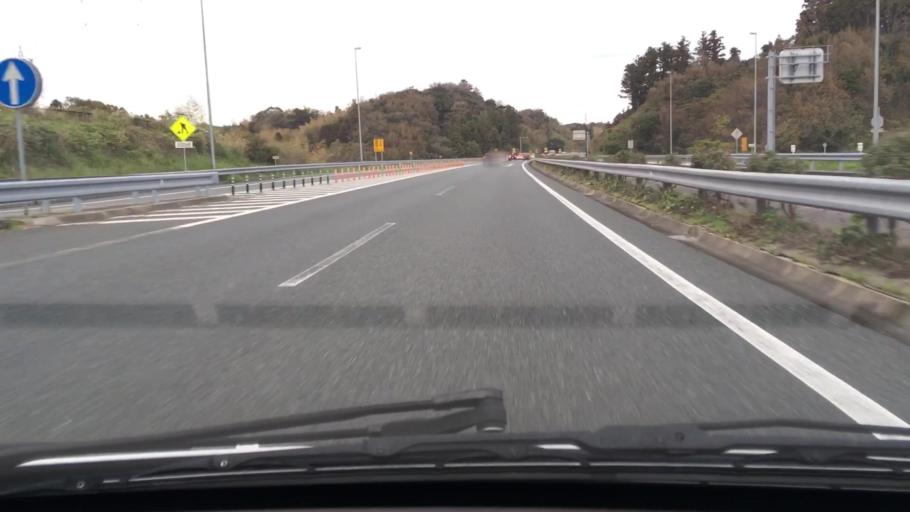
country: JP
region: Chiba
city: Kimitsu
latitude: 35.2533
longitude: 139.8926
